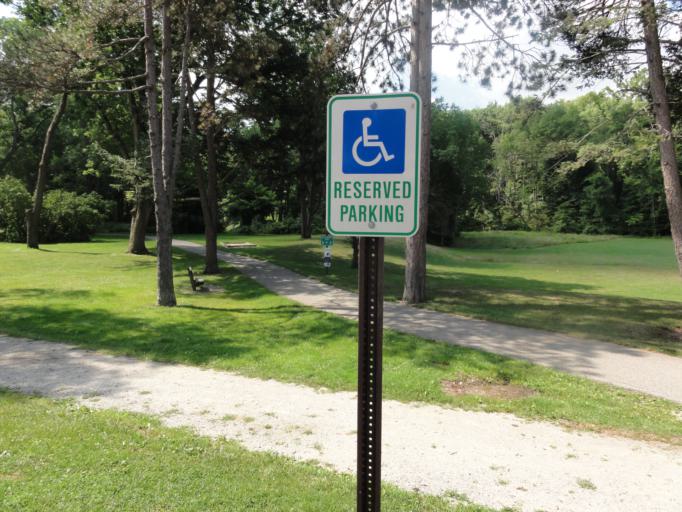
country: US
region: Ohio
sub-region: Cuyahoga County
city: Moreland Hills
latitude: 41.4228
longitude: -81.4172
